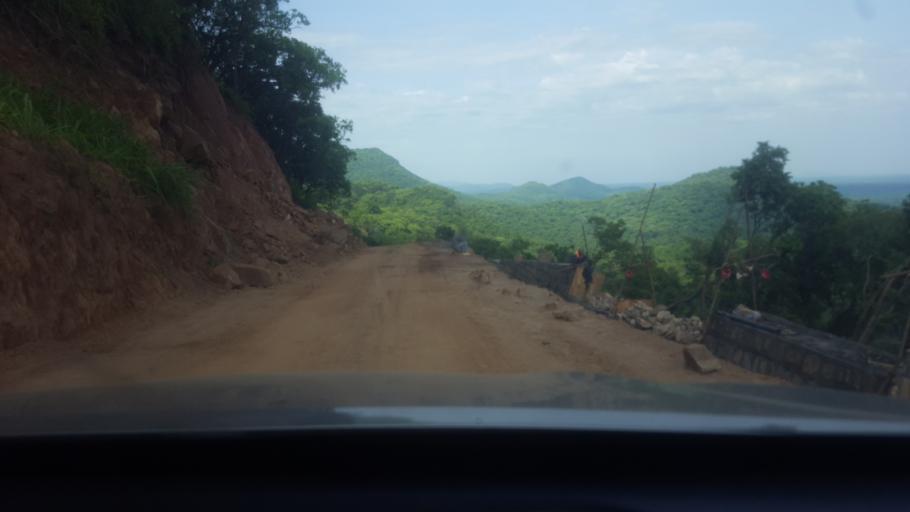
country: ET
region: Southern Nations, Nationalities, and People's Region
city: Tippi
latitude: 7.5404
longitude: 34.9754
